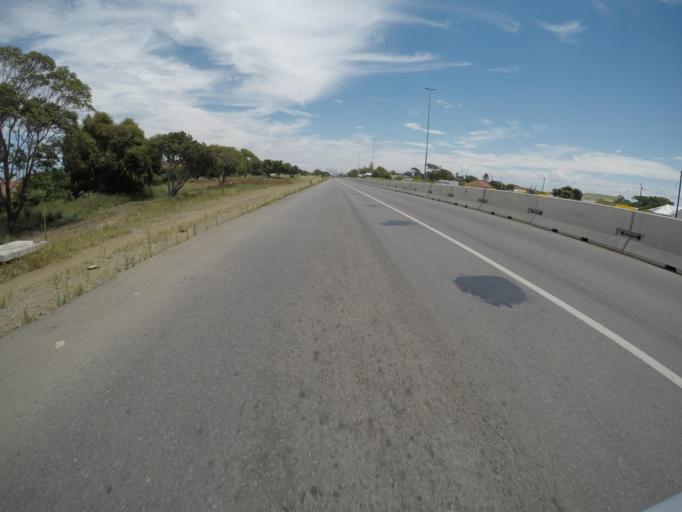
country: ZA
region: Eastern Cape
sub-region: Buffalo City Metropolitan Municipality
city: East London
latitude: -33.0360
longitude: 27.8542
